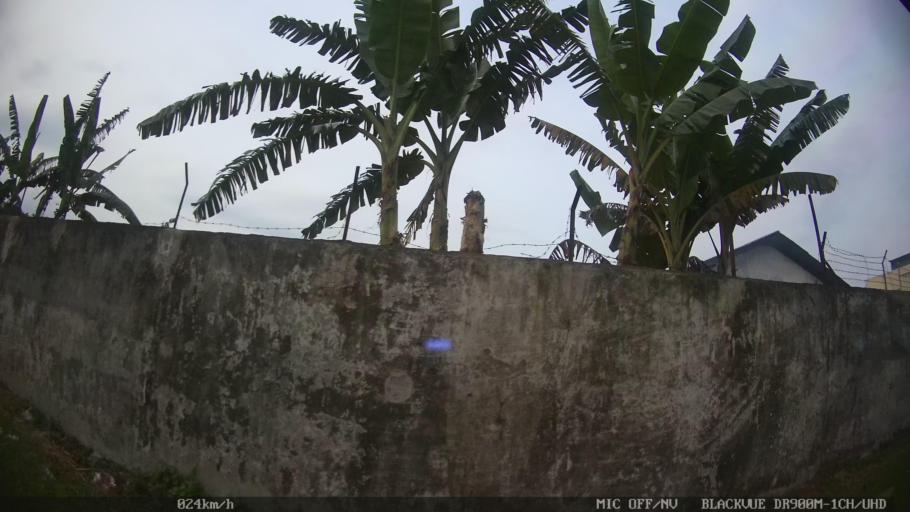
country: ID
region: North Sumatra
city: Sunggal
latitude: 3.5811
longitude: 98.6035
